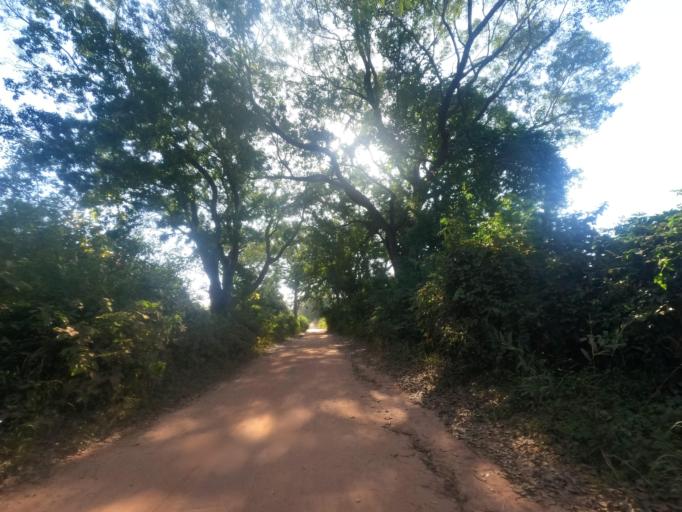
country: GW
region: Cacheu
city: Cacheu
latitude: 12.3970
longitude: -16.2139
